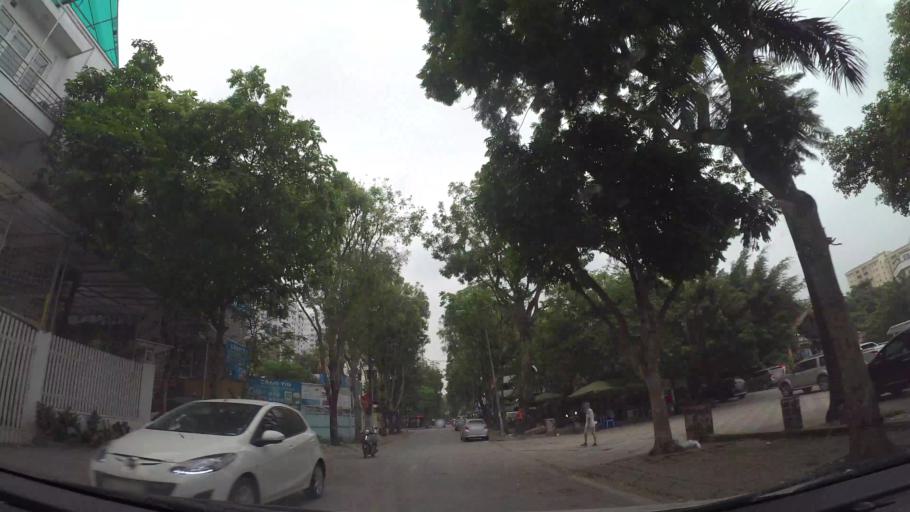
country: VN
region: Ha Noi
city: Cau Dien
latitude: 21.0313
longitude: 105.7662
